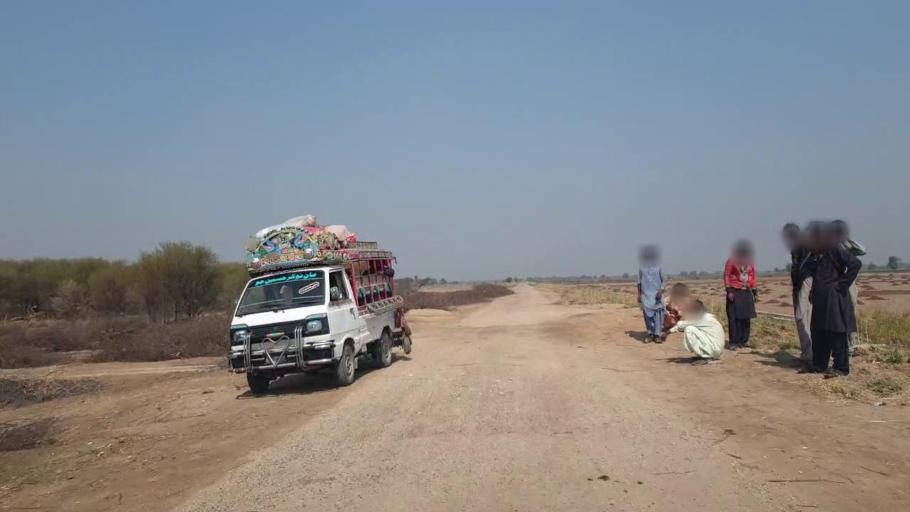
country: PK
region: Sindh
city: Mirwah Gorchani
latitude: 25.3619
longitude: 68.9316
